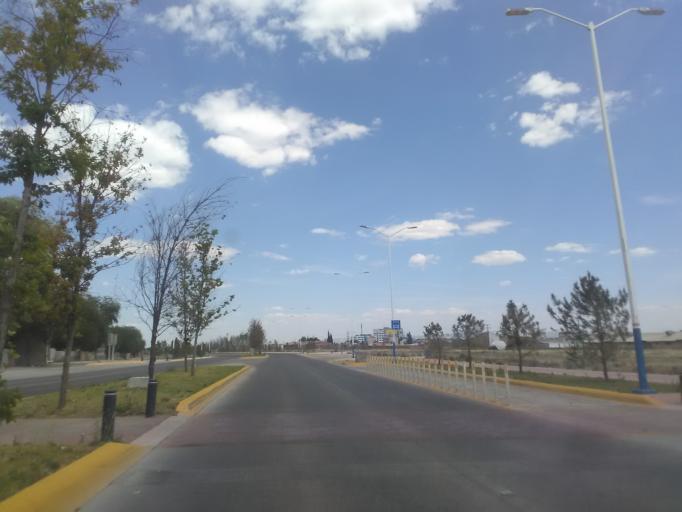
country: MX
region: Durango
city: Victoria de Durango
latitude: 24.0366
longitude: -104.6711
